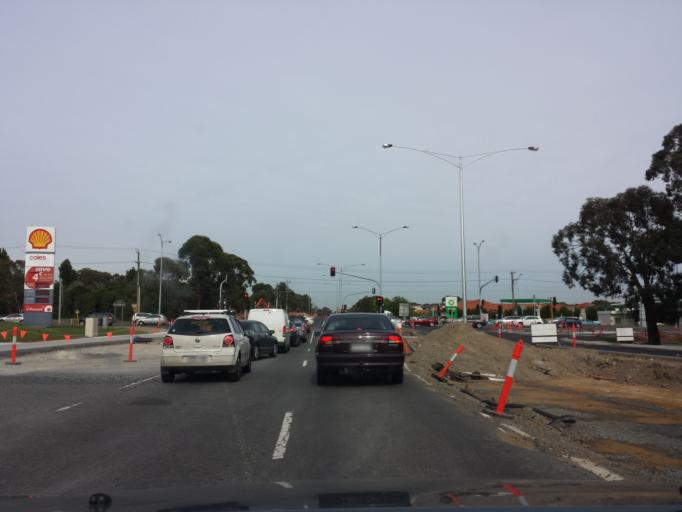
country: AU
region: Victoria
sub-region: Knox
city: Wantirna South
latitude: -37.8770
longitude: 145.2340
